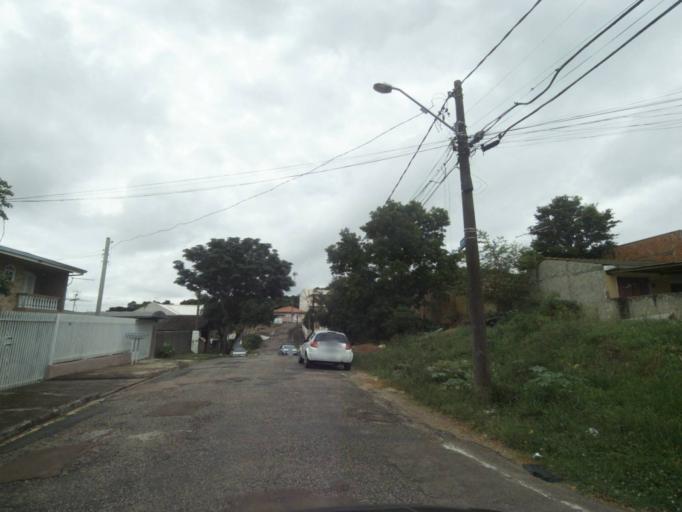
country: BR
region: Parana
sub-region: Curitiba
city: Curitiba
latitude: -25.4744
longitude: -49.3323
